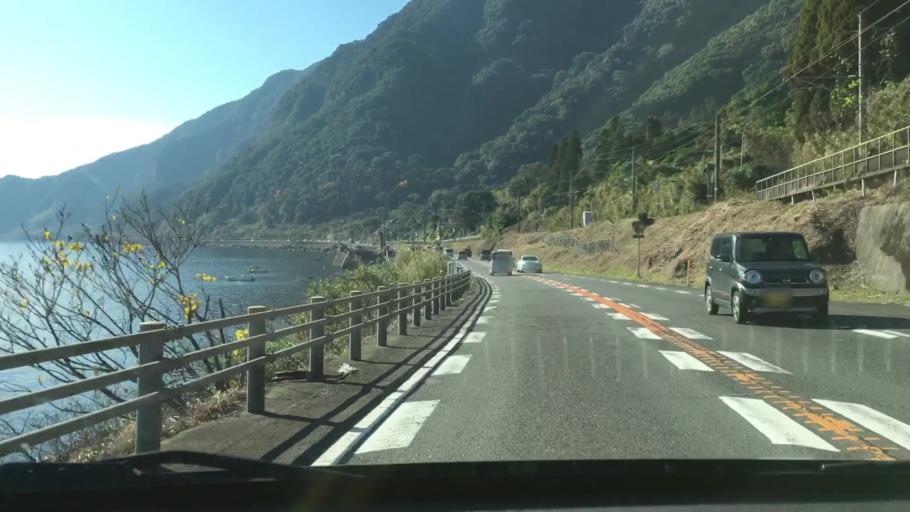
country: JP
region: Kagoshima
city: Kajiki
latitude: 31.6855
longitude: 130.6102
